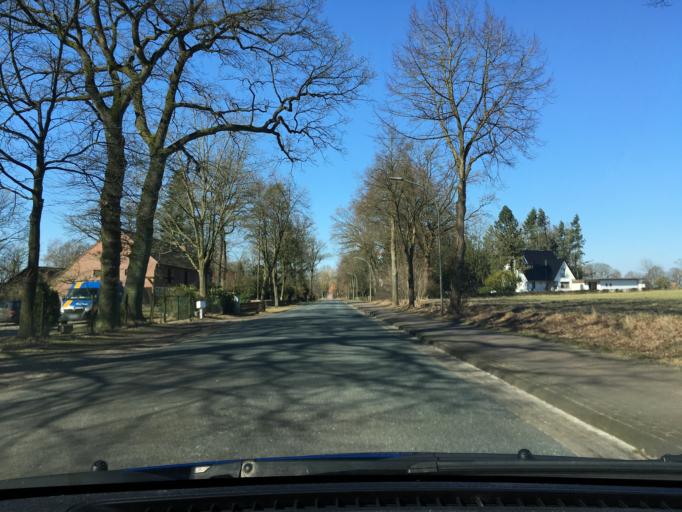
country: DE
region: Lower Saxony
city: Hemslingen
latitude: 53.0690
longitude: 9.6494
